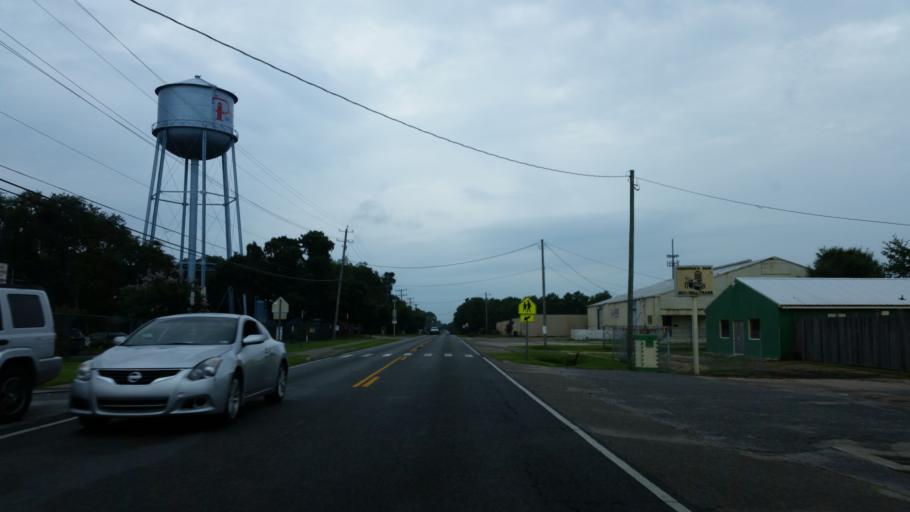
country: US
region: Florida
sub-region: Escambia County
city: Warrington
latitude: 30.4049
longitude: -87.2743
